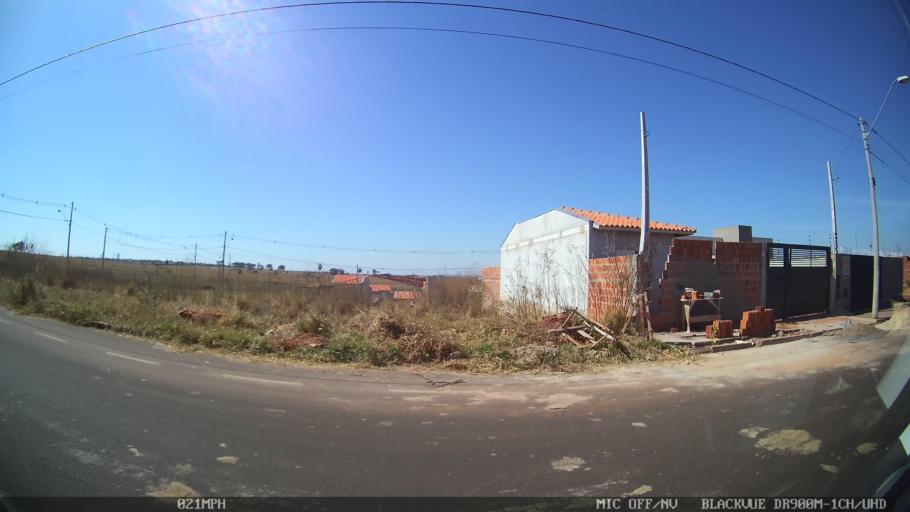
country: BR
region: Sao Paulo
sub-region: Sao Jose Do Rio Preto
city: Sao Jose do Rio Preto
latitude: -20.7519
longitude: -49.4251
